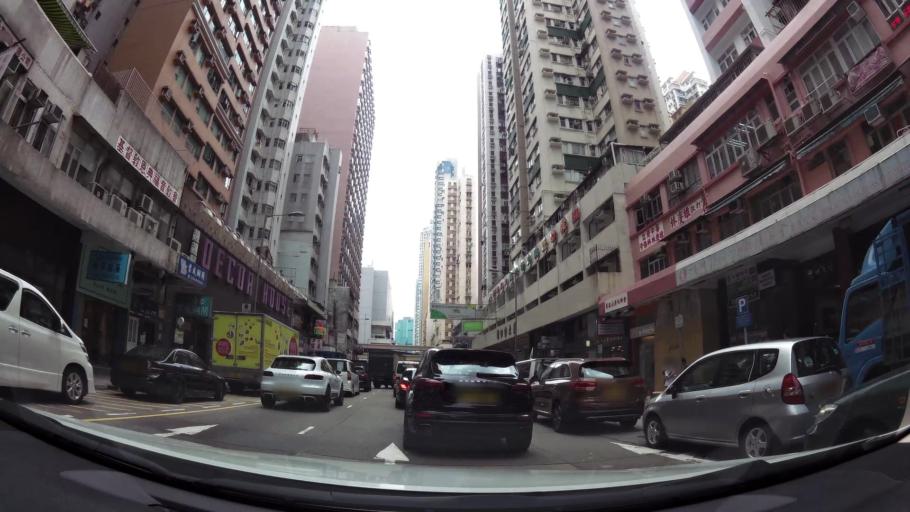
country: HK
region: Wanchai
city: Wan Chai
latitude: 22.2915
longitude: 114.1972
